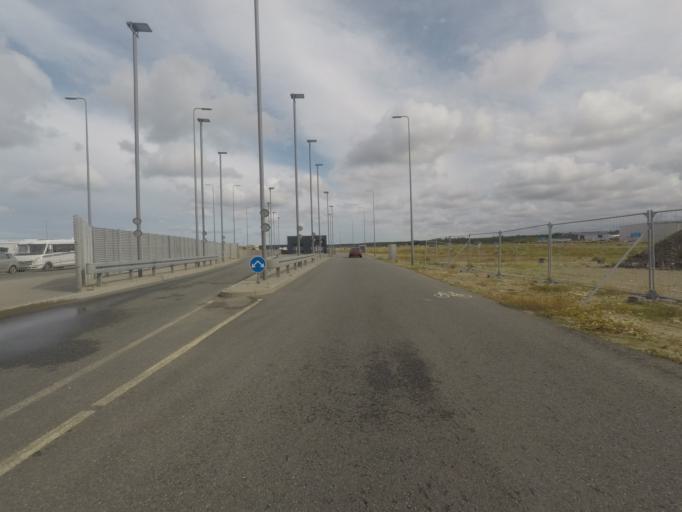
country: DK
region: North Denmark
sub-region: Hjorring Kommune
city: Hirtshals
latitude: 57.5916
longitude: 9.9944
